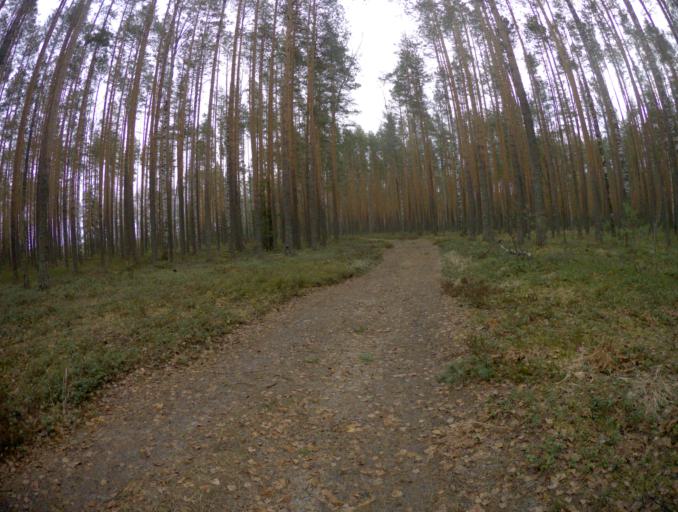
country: RU
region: Vladimir
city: Raduzhnyy
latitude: 55.9474
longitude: 40.2846
